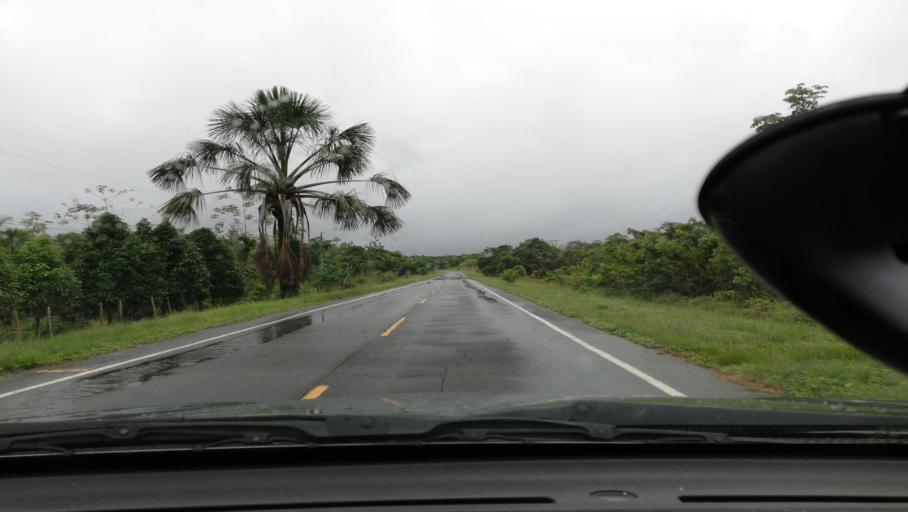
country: PE
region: Loreto
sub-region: Provincia de Loreto
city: Nauta
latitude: -4.2113
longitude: -73.4822
